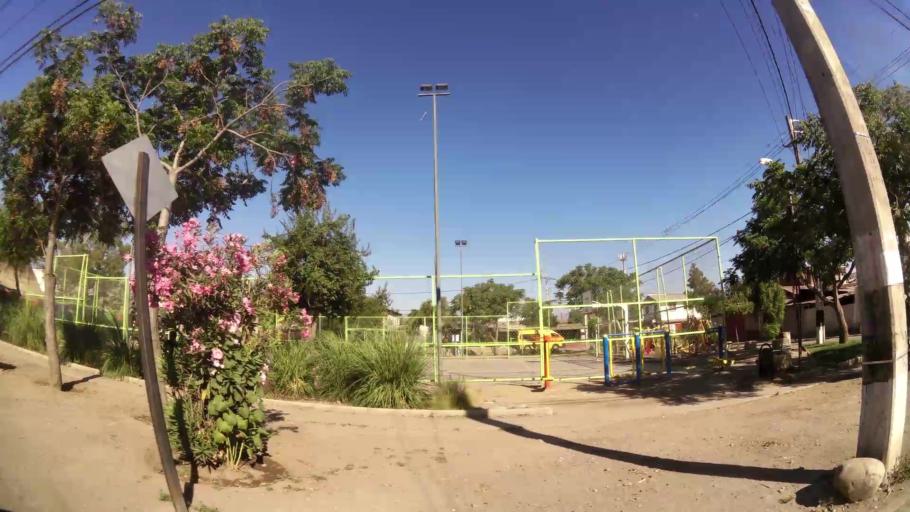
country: CL
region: Santiago Metropolitan
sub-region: Provincia de Maipo
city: San Bernardo
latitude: -33.5882
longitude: -70.6819
